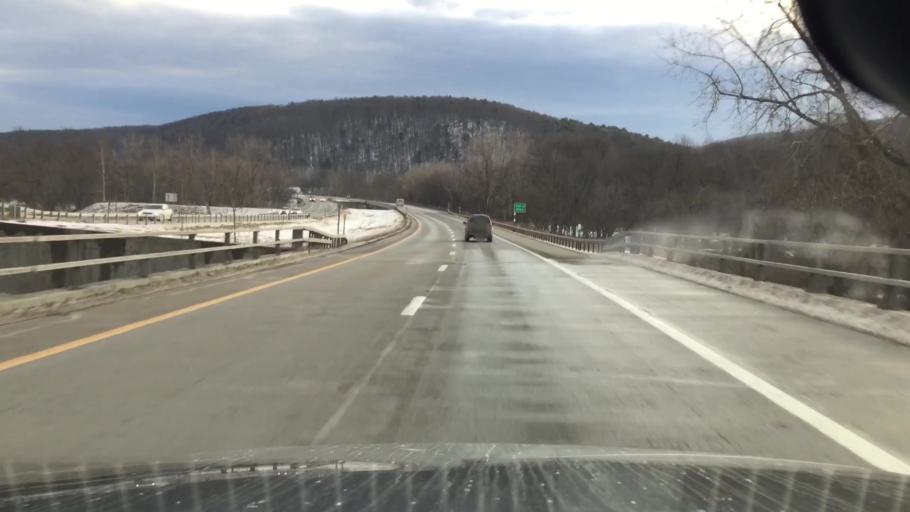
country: US
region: Pennsylvania
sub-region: Bradford County
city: Sayre
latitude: 42.0074
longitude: -76.4673
